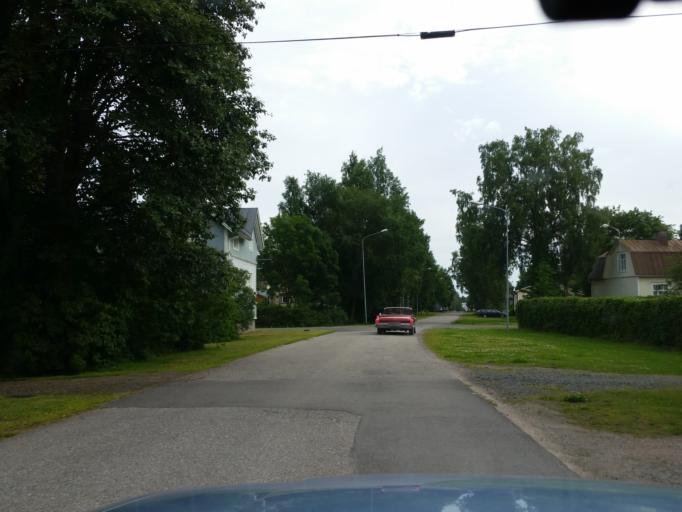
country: FI
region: Uusimaa
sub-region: Raaseporin
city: Hanko
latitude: 59.8368
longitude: 22.9543
